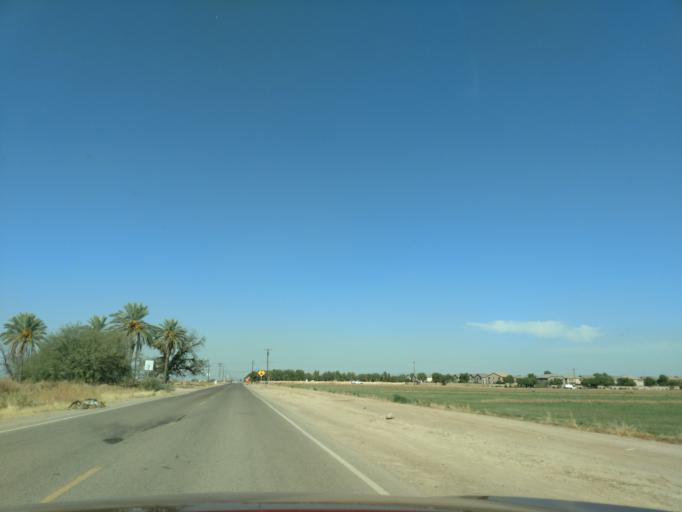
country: US
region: Arizona
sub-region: Maricopa County
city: Laveen
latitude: 33.3605
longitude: -112.1863
